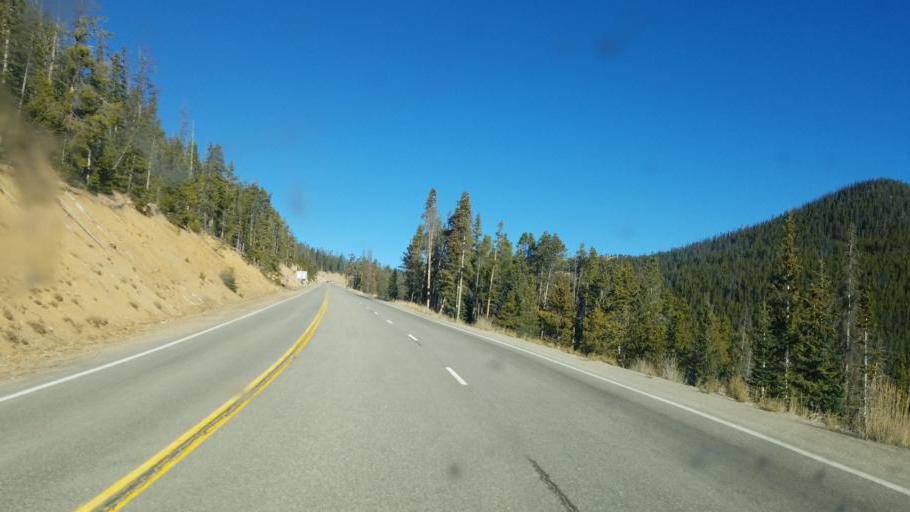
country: US
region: Colorado
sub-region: Chaffee County
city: Salida
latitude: 38.4782
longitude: -106.3356
